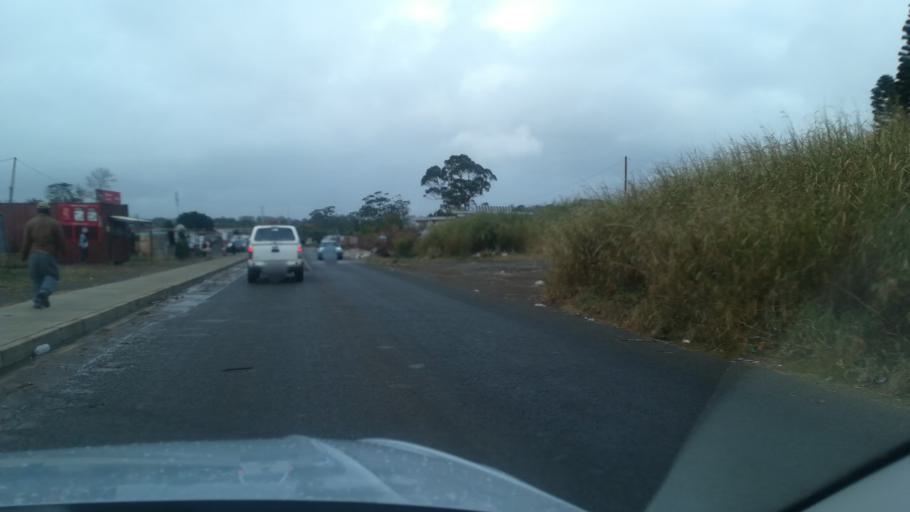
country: ZA
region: Eastern Cape
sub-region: Buffalo City Metropolitan Municipality
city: East London
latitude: -33.0010
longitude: 27.8383
